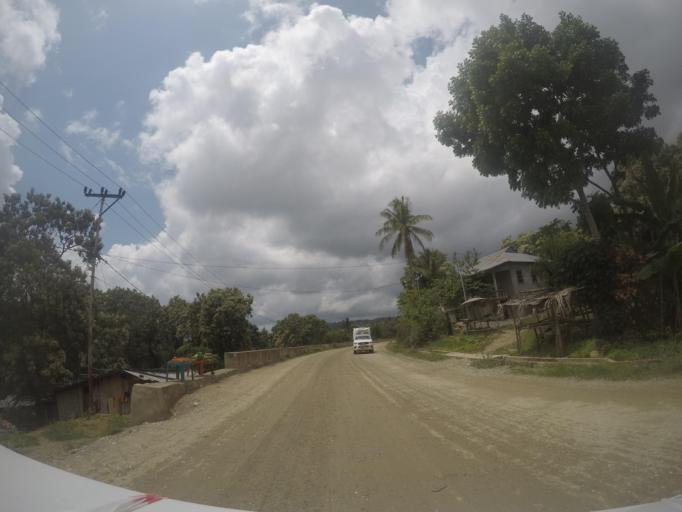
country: TL
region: Baucau
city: Venilale
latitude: -8.5841
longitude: 126.3899
